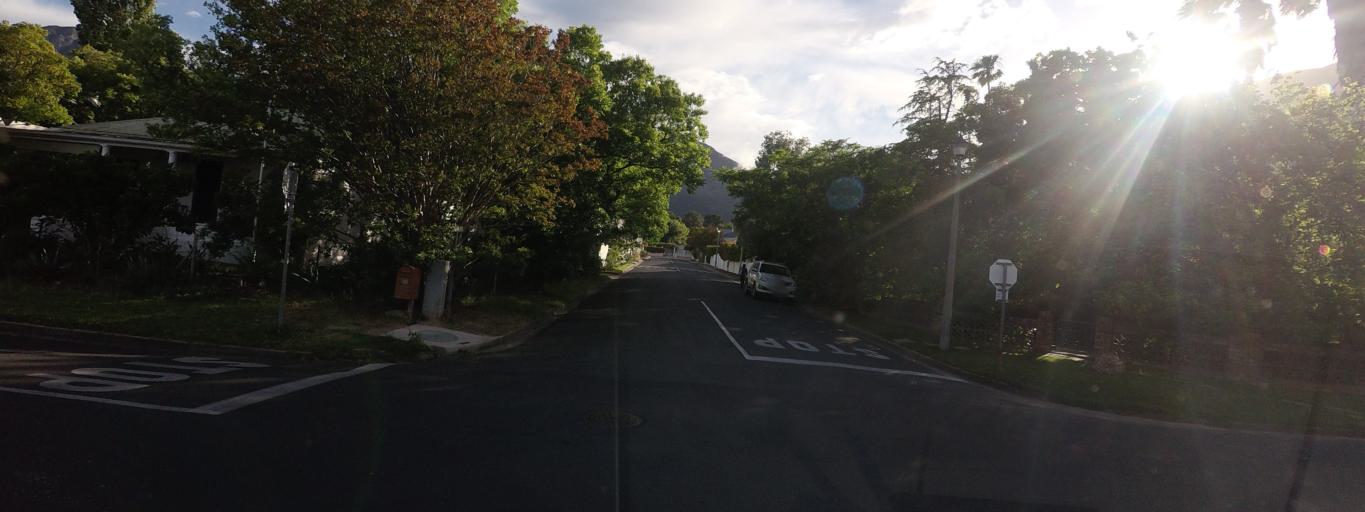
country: ZA
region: Western Cape
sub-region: Cape Winelands District Municipality
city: Paarl
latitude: -33.9122
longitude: 19.1221
